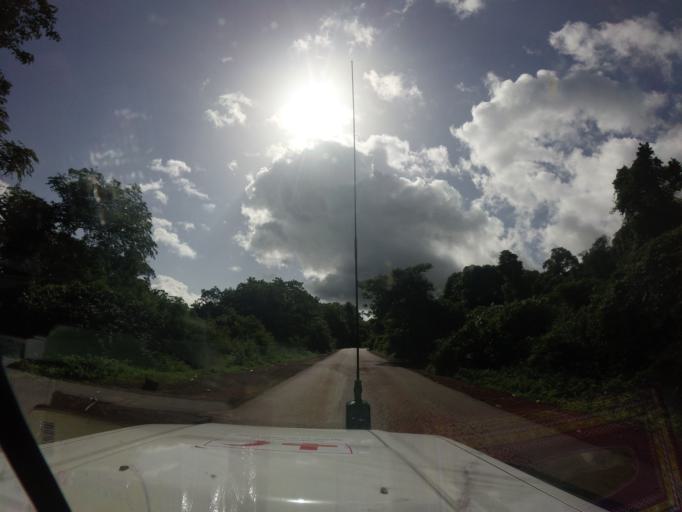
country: GN
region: Mamou
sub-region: Mamou Prefecture
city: Mamou
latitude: 10.3522
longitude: -12.1907
